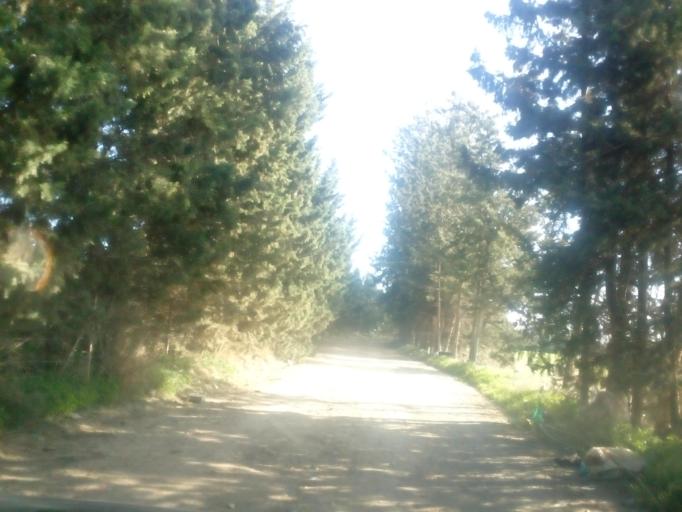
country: CY
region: Limassol
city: Ypsonas
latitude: 34.6608
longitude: 32.9758
